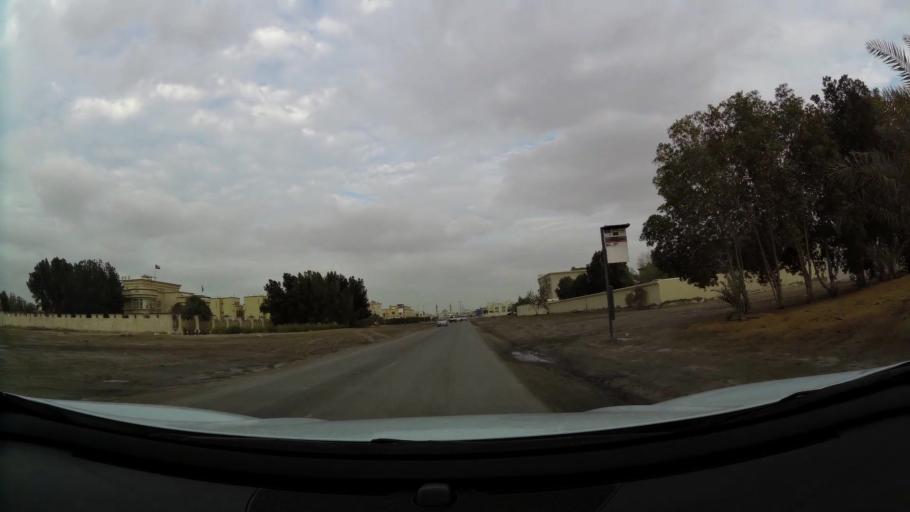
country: AE
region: Abu Dhabi
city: Abu Dhabi
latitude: 24.3527
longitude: 54.5501
